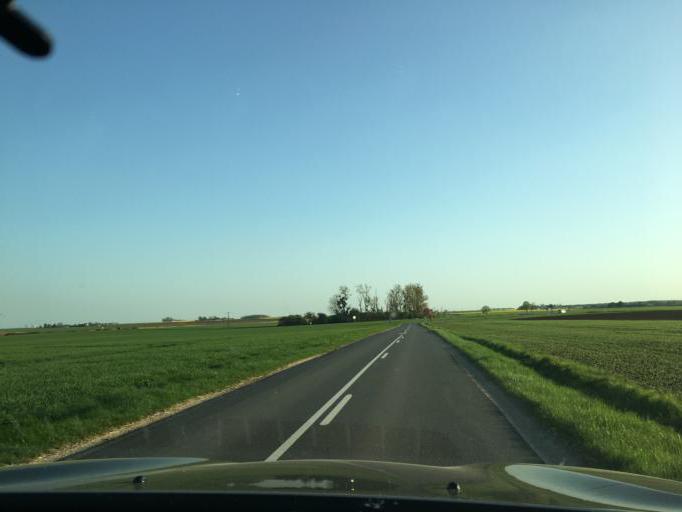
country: FR
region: Centre
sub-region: Departement du Loir-et-Cher
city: Ouzouer-le-Marche
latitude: 47.8569
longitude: 1.5238
